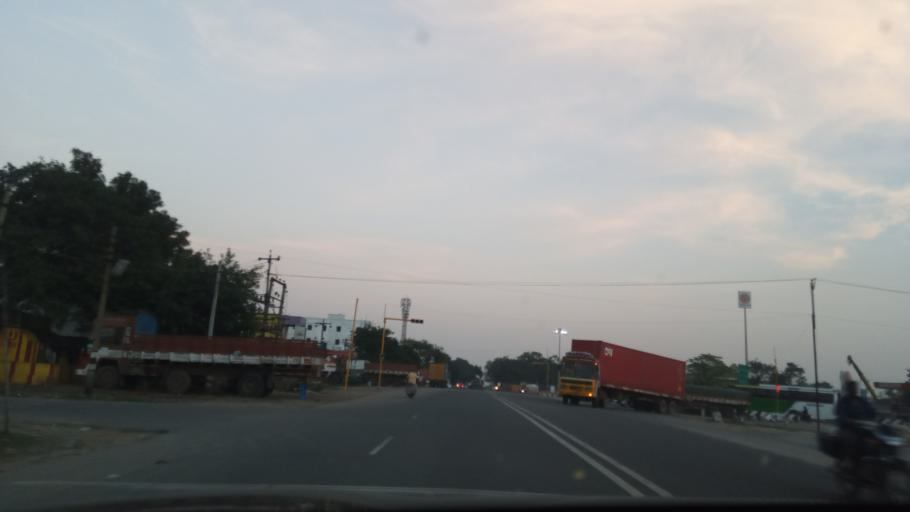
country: IN
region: Tamil Nadu
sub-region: Vellore
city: Walajapet
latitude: 12.9273
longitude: 79.3477
